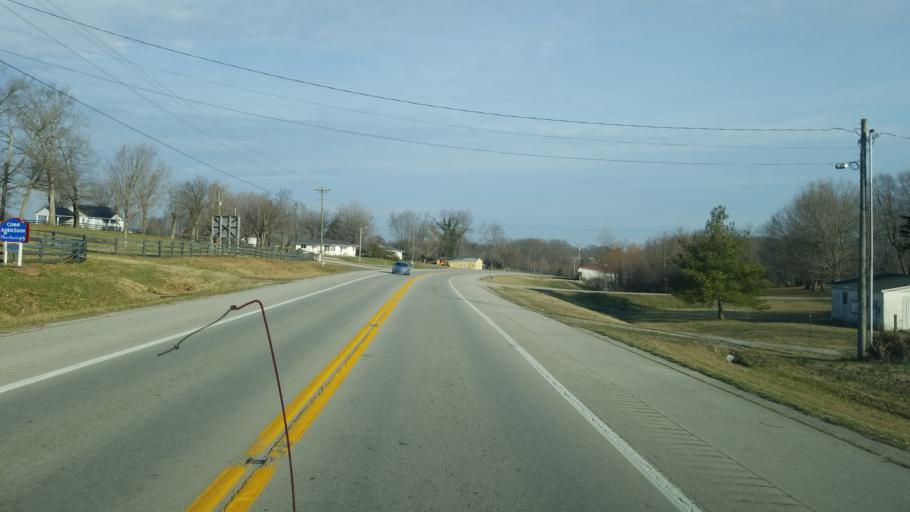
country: US
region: Kentucky
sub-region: Russell County
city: Russell Springs
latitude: 37.0740
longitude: -85.0716
